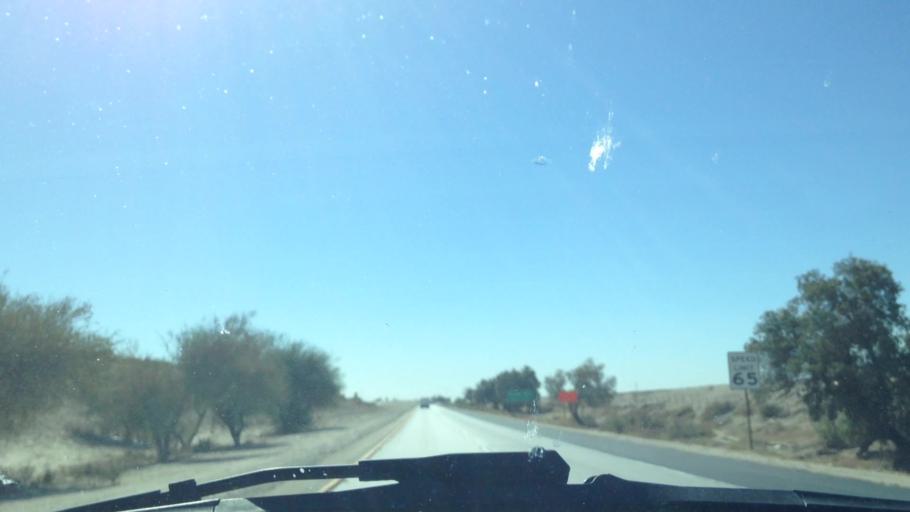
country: US
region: California
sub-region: Riverside County
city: Indio
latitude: 33.7156
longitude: -116.1910
